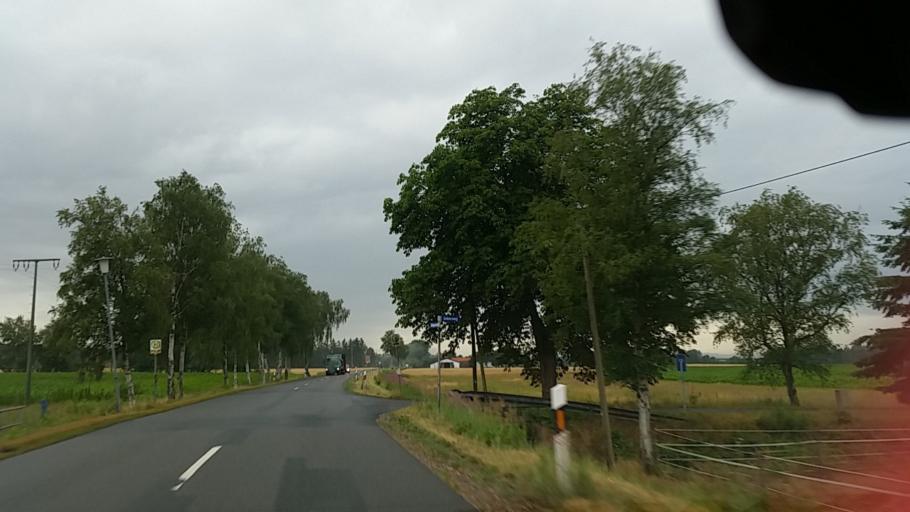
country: DE
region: Lower Saxony
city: Schoneworde
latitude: 52.6051
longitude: 10.6886
